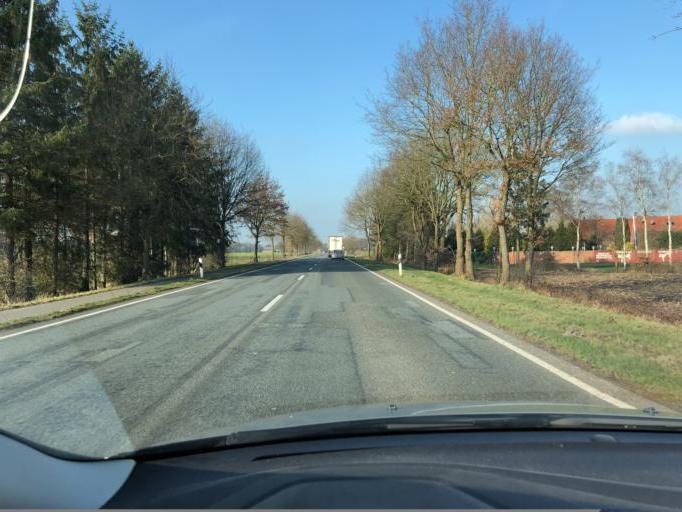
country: DE
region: Lower Saxony
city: Apen
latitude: 53.2966
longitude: 7.8214
